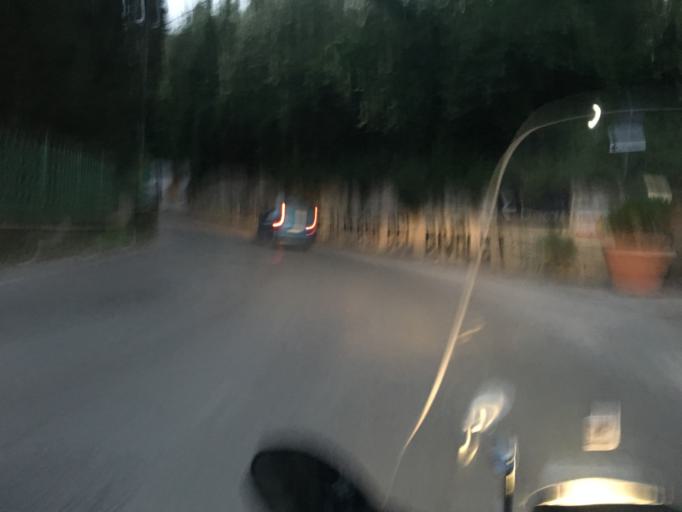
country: IT
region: Campania
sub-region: Provincia di Napoli
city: Napoli
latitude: 40.8638
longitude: 14.2150
